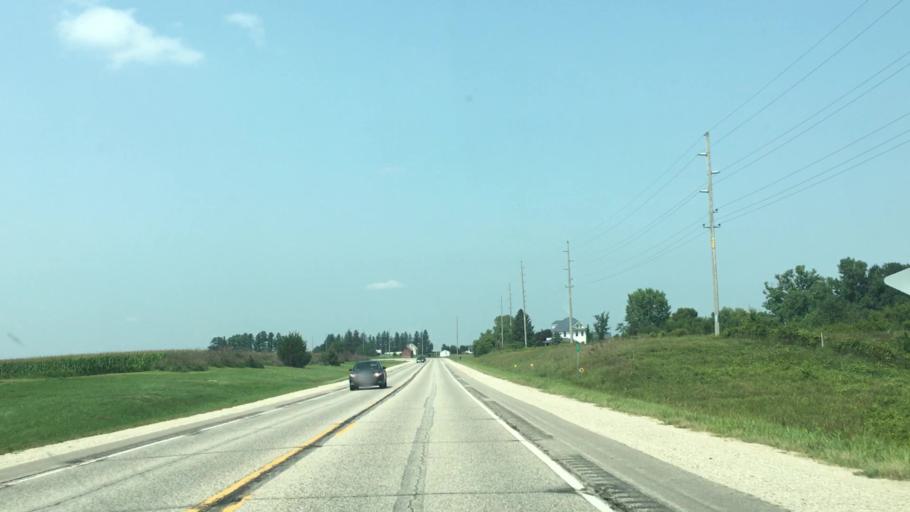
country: US
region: Iowa
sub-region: Fayette County
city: Fayette
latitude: 42.9004
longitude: -91.8104
